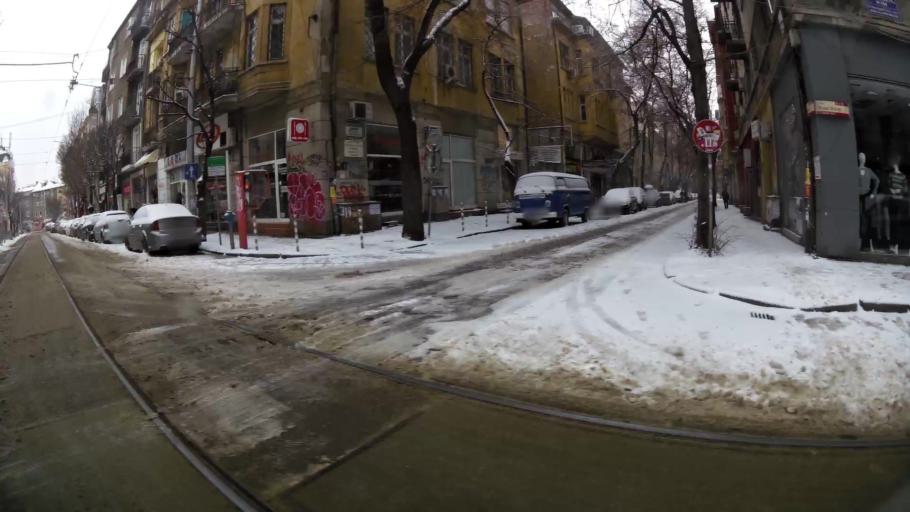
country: BG
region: Sofia-Capital
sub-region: Stolichna Obshtina
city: Sofia
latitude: 42.7007
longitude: 23.3200
